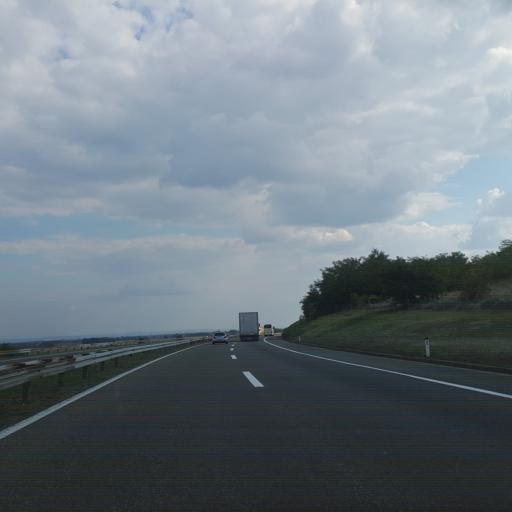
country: RS
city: Lugavcina
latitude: 44.5277
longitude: 21.0065
